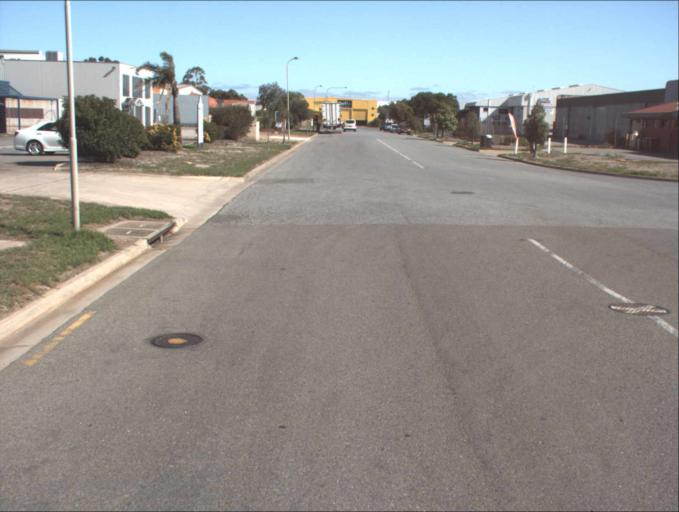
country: AU
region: South Australia
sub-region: Port Adelaide Enfield
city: Blair Athol
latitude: -34.8449
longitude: 138.5678
